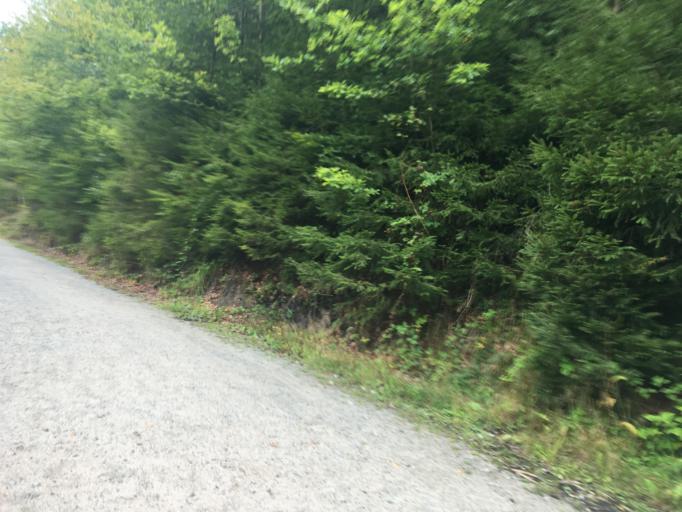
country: DE
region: Saxony
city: Bad Schandau
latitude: 50.9177
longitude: 14.2279
